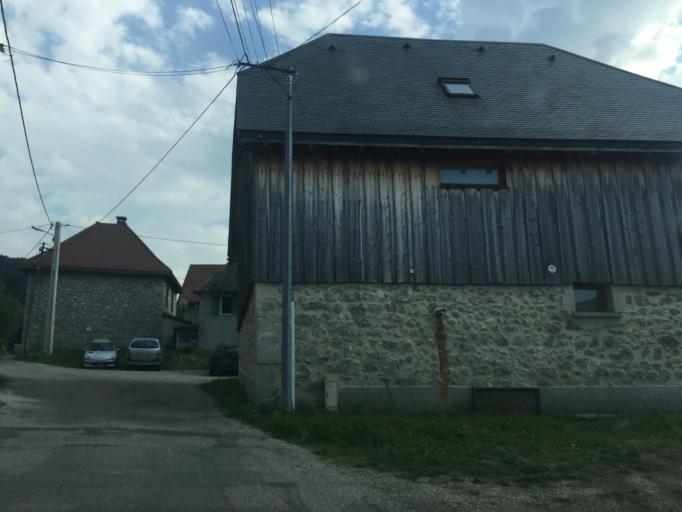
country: FR
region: Rhone-Alpes
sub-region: Departement de l'Isere
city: Le Sappey-en-Chartreuse
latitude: 45.3161
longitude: 5.8088
